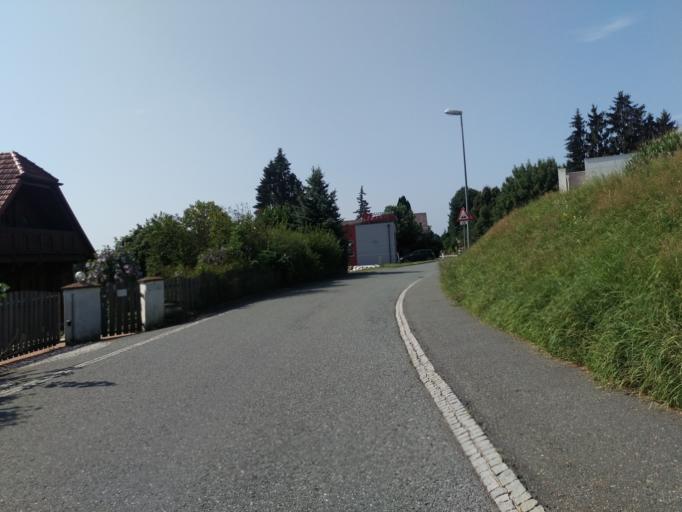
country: AT
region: Styria
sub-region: Politischer Bezirk Graz-Umgebung
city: Mellach
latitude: 46.9311
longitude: 15.5115
